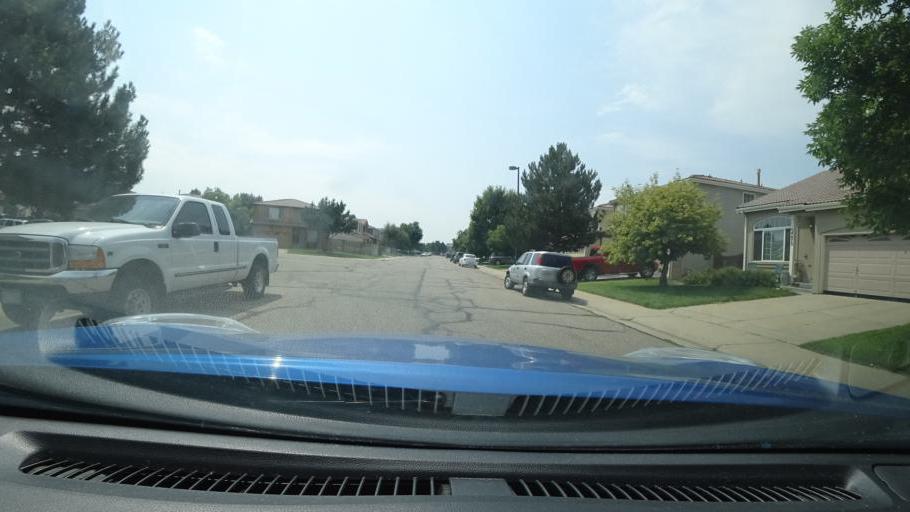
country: US
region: Colorado
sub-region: Adams County
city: Aurora
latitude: 39.7815
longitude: -104.7573
